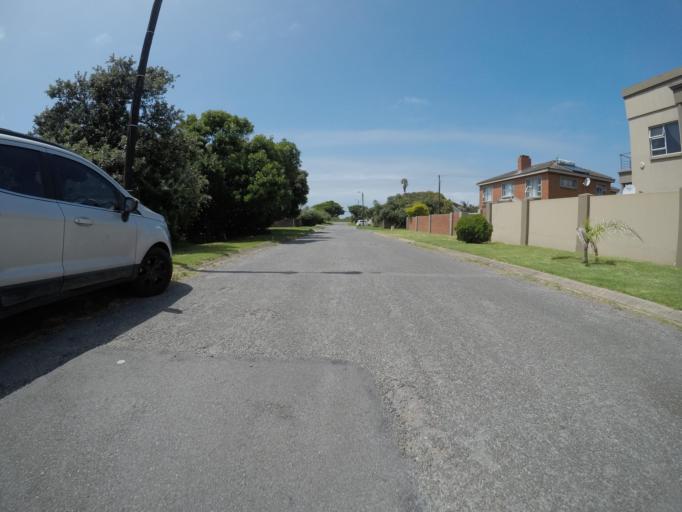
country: ZA
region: Eastern Cape
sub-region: Buffalo City Metropolitan Municipality
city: East London
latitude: -32.9475
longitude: 28.0201
